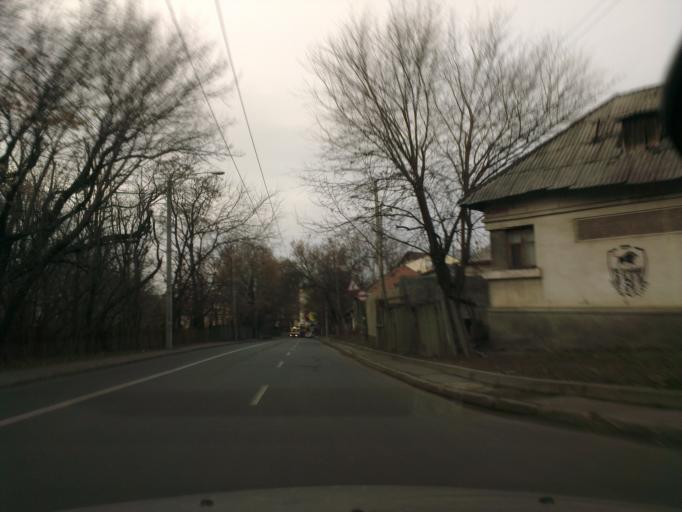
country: MD
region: Chisinau
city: Chisinau
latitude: 47.0310
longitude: 28.8168
